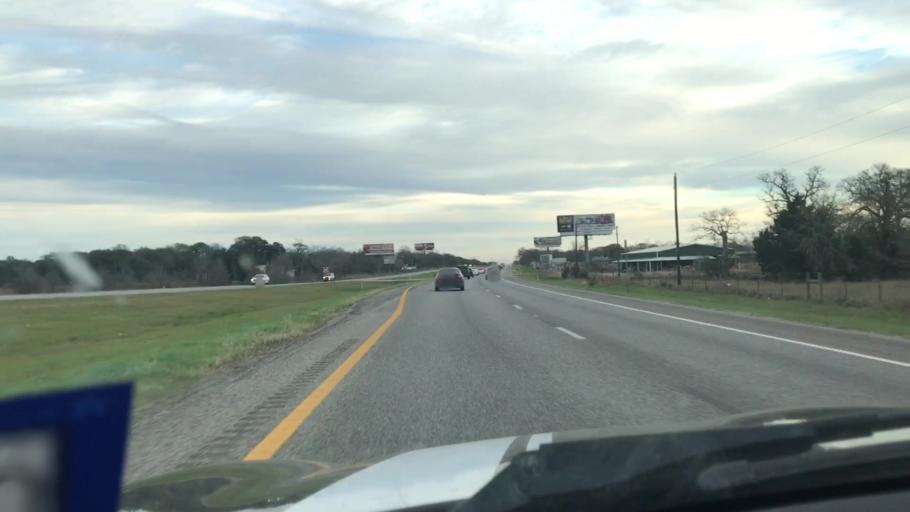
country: US
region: Texas
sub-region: Waller County
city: Hempstead
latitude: 30.1298
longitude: -96.1391
